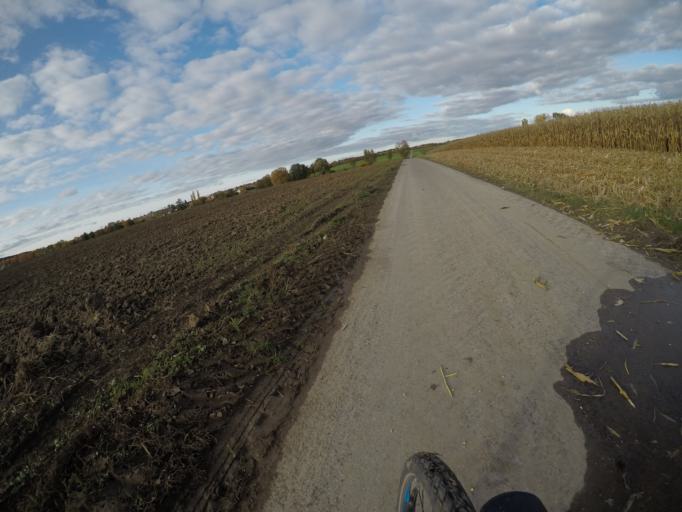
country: DE
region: Baden-Wuerttemberg
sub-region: Regierungsbezirk Stuttgart
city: Leinfelden-Echterdingen
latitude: 48.6746
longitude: 9.1731
